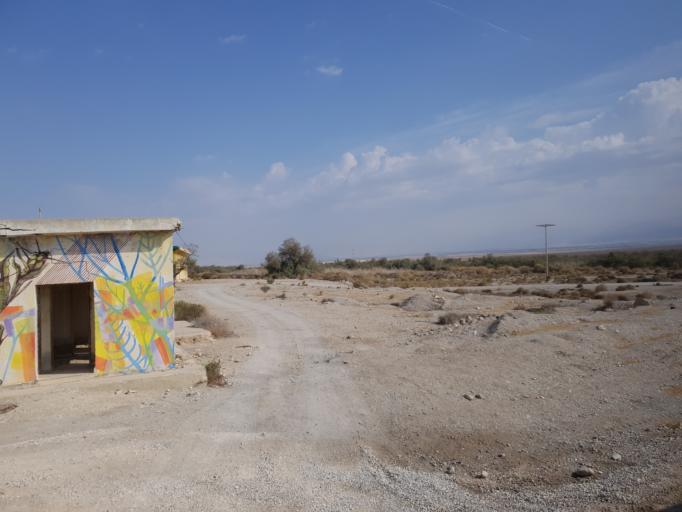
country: PS
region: West Bank
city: Jericho
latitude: 31.7653
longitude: 35.4993
